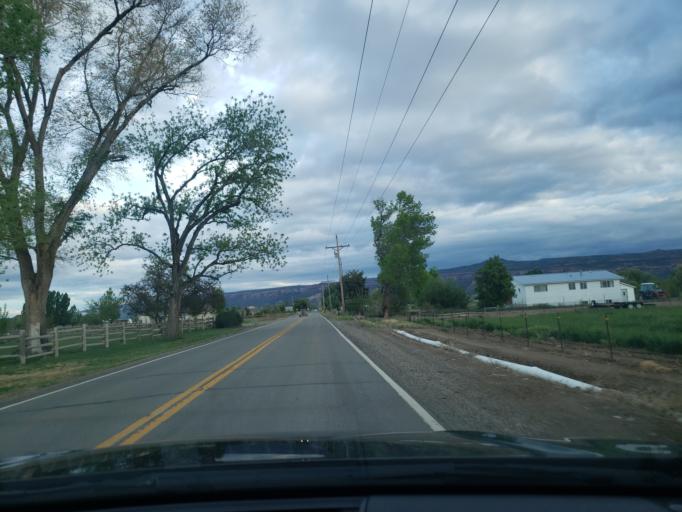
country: US
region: Colorado
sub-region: Mesa County
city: Fruita
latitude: 39.1685
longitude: -108.7012
